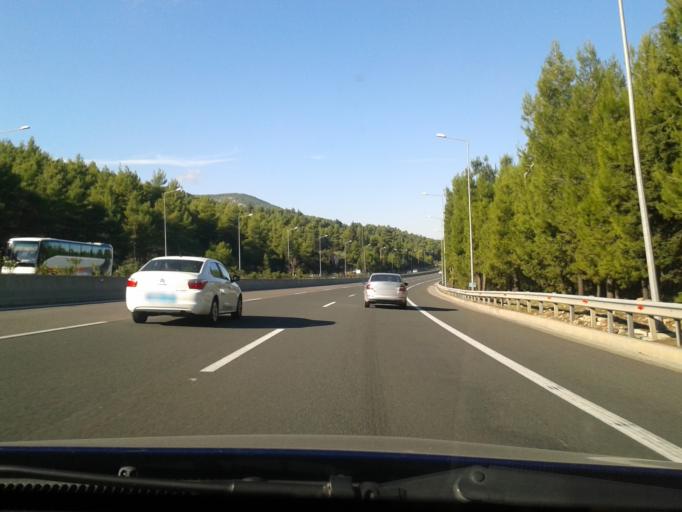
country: GR
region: Attica
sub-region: Nomarchia Anatolikis Attikis
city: Afidnes
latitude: 38.2290
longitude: 23.8064
